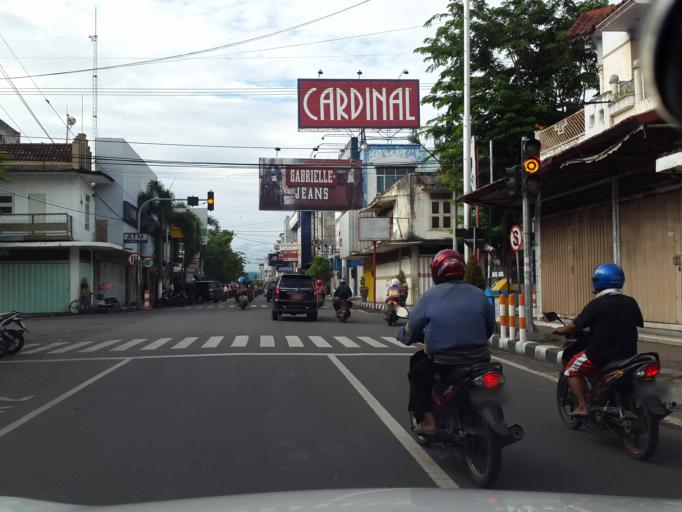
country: ID
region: East Java
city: Mojokerto
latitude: -7.4657
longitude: 112.4319
